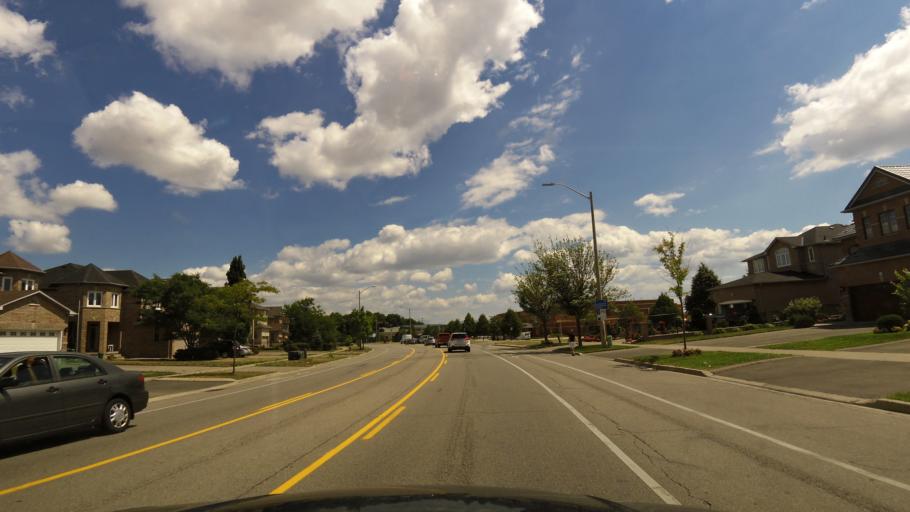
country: CA
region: Ontario
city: Mississauga
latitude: 43.6157
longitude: -79.6568
